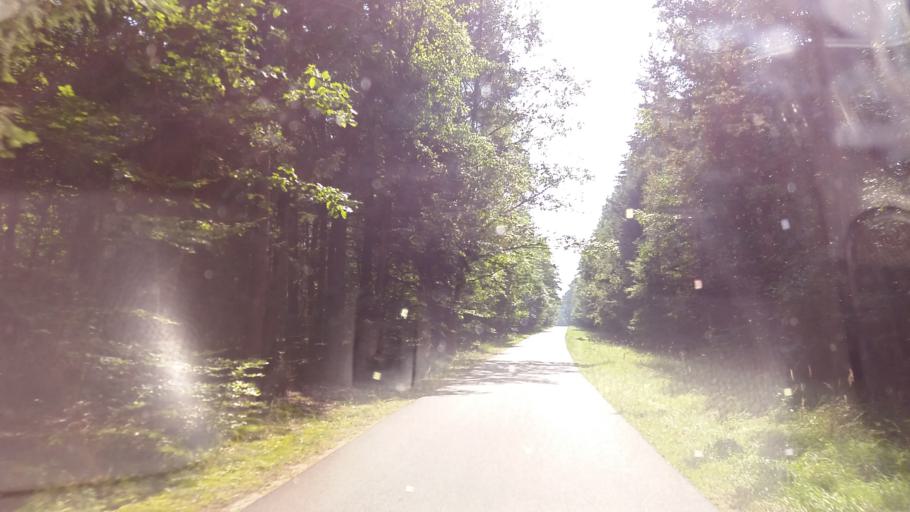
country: PL
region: West Pomeranian Voivodeship
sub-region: Powiat walecki
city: Czlopa
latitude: 53.0973
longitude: 15.9315
